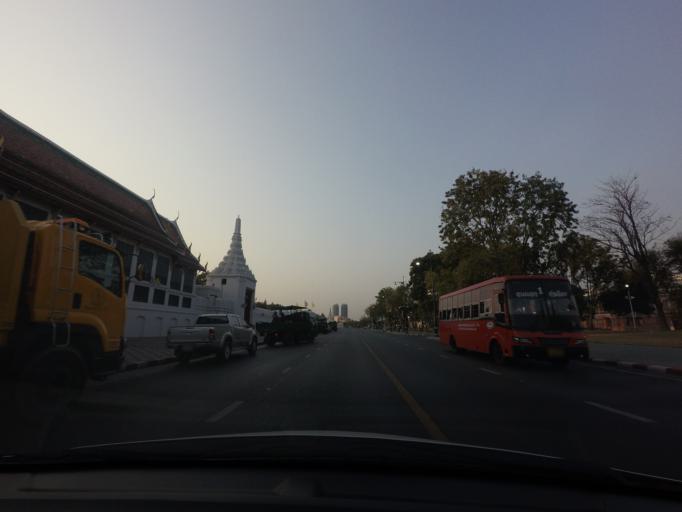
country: TH
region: Bangkok
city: Bangkok
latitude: 13.7494
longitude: 100.4940
